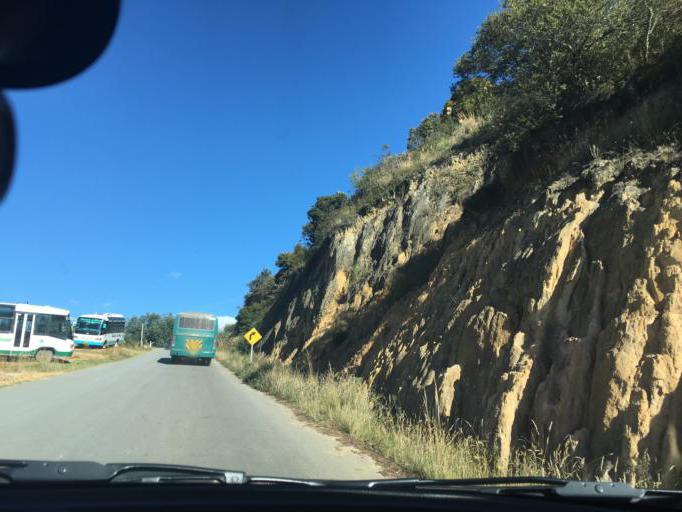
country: CO
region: Boyaca
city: Aquitania
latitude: 5.5103
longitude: -72.9715
